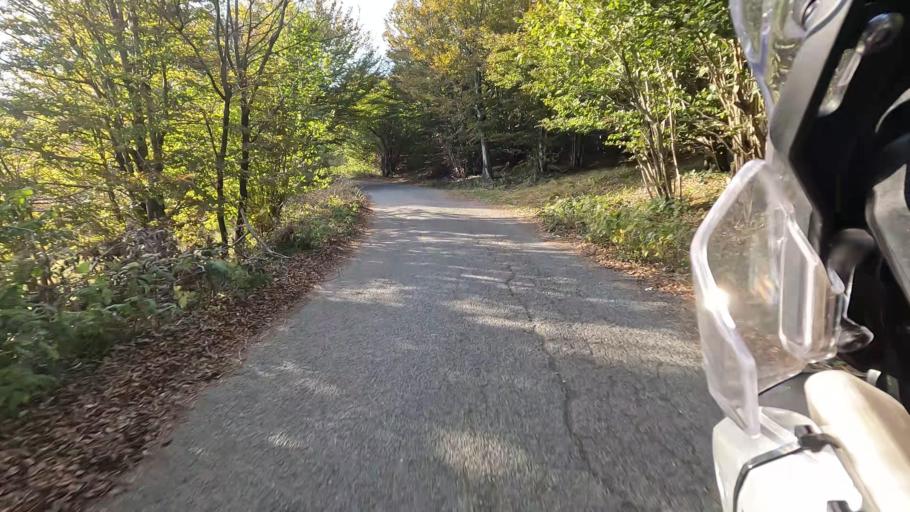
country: IT
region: Liguria
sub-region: Provincia di Genova
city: Sciarborasca
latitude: 44.4302
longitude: 8.5834
